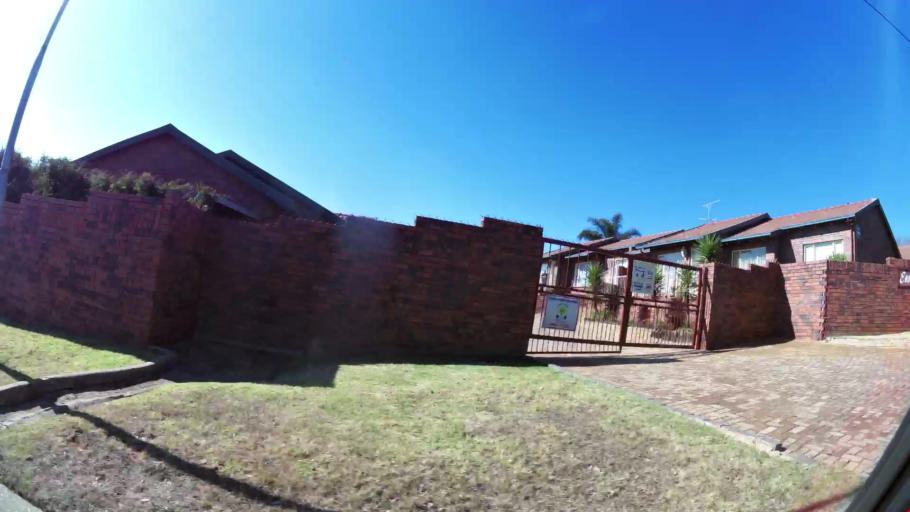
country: ZA
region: Gauteng
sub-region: City of Johannesburg Metropolitan Municipality
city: Roodepoort
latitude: -26.1216
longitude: 27.8454
